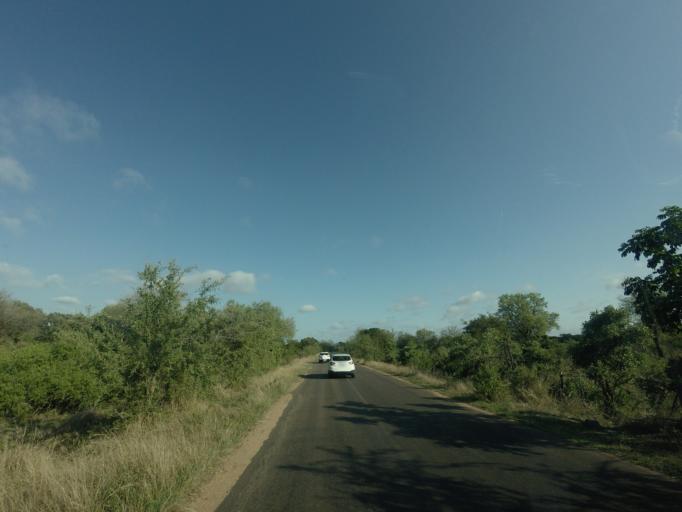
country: ZA
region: Mpumalanga
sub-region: Ehlanzeni District
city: Komatipoort
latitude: -25.2765
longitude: 31.8493
